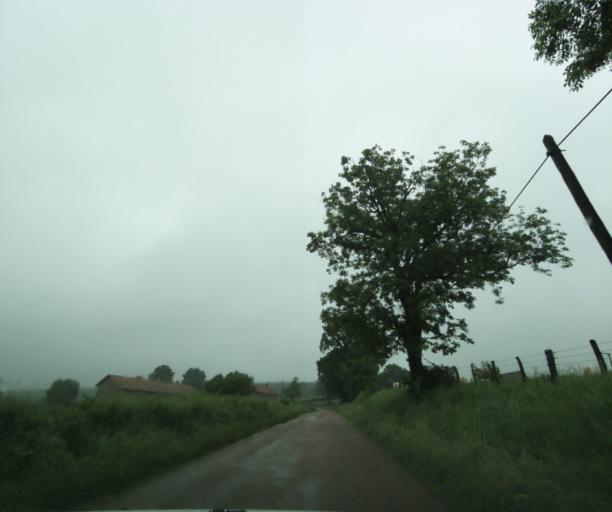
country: FR
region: Bourgogne
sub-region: Departement de Saone-et-Loire
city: Charolles
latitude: 46.4018
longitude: 4.3507
